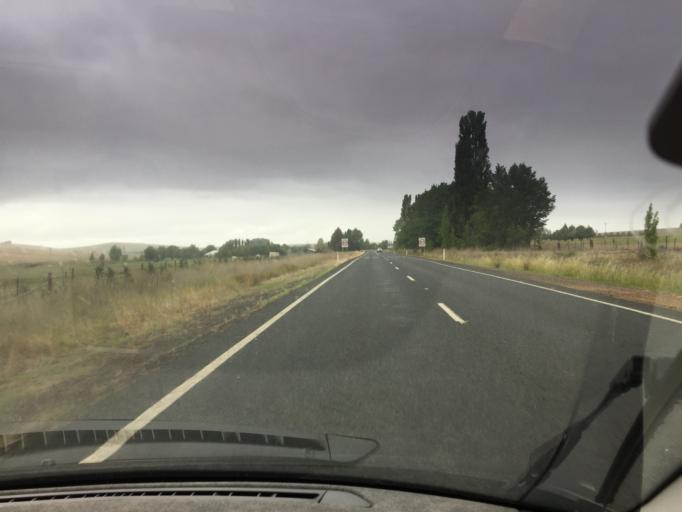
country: AU
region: New South Wales
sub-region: Cooma-Monaro
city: Cooma
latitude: -36.2021
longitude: 149.1580
